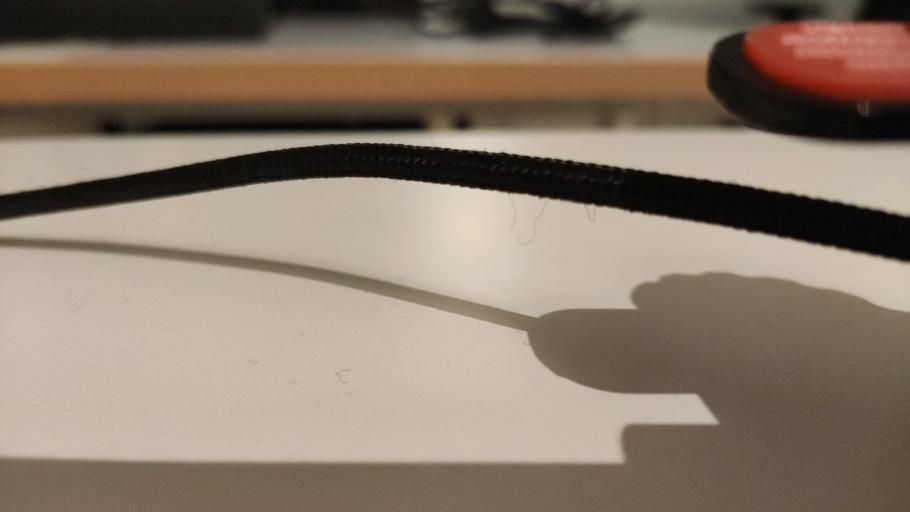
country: RU
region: Moskovskaya
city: Rogachevo
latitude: 56.4342
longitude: 37.1806
